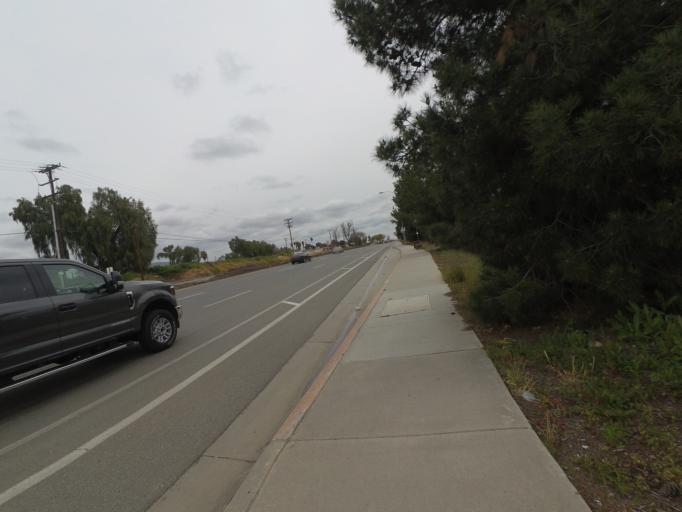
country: US
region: California
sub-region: Riverside County
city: March Air Force Base
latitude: 33.9167
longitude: -117.2786
